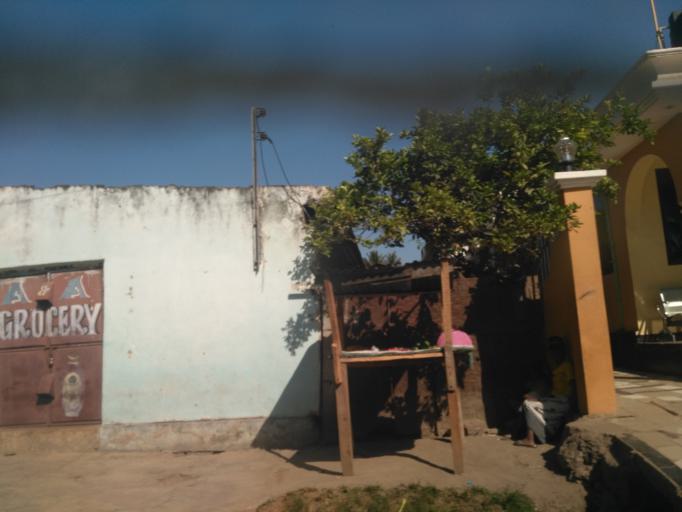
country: TZ
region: Mwanza
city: Mwanza
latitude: -2.5024
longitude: 32.8970
